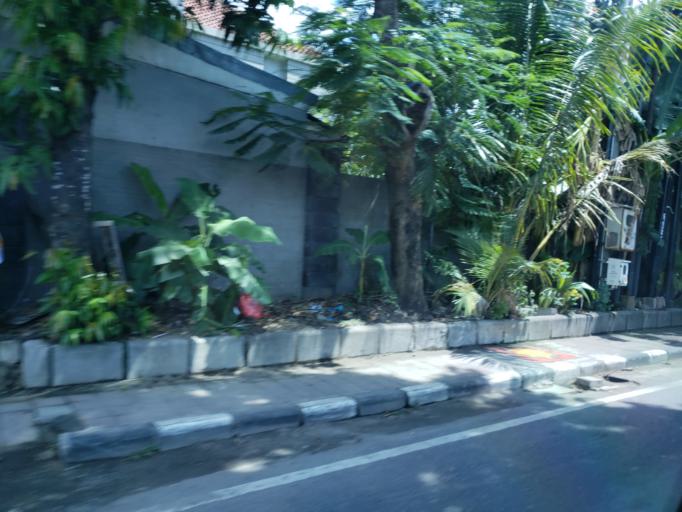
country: ID
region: Bali
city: Kelanabian
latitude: -8.7589
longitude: 115.1764
